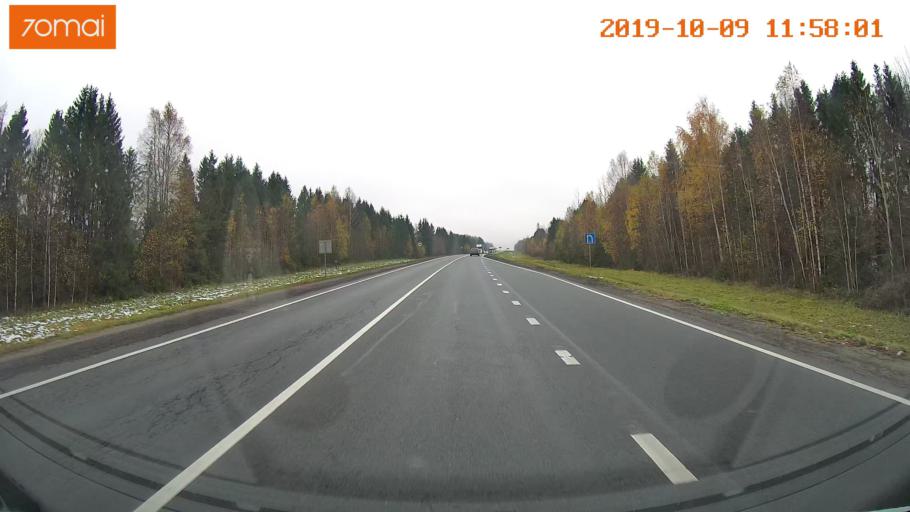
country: RU
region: Vologda
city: Gryazovets
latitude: 58.7241
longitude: 40.2957
